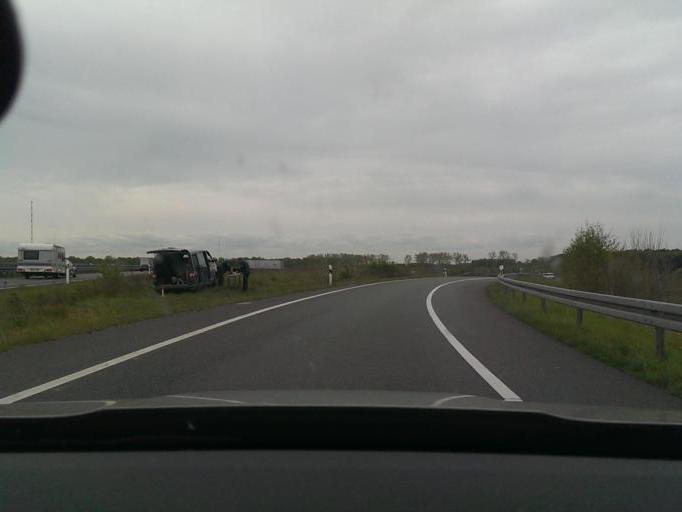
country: DE
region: Lower Saxony
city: Lehre
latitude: 52.3114
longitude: 10.7283
